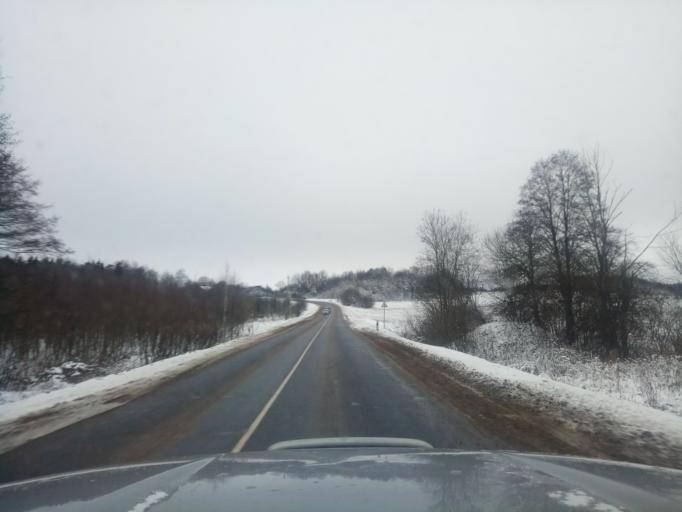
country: BY
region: Minsk
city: Kapyl'
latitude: 53.1526
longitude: 27.1206
